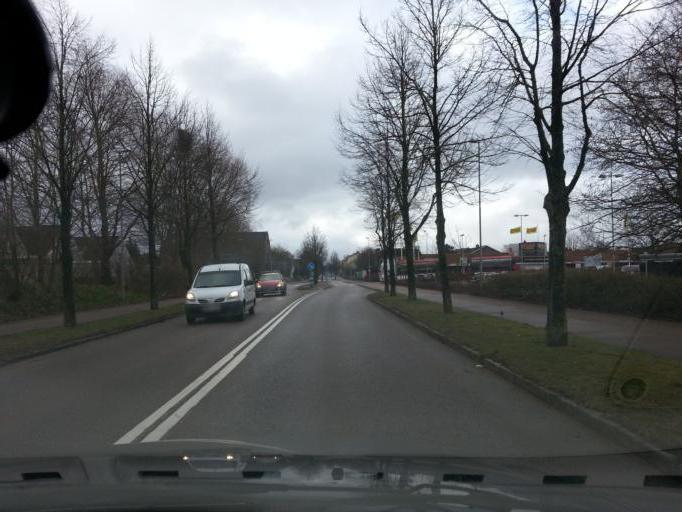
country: SE
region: Skane
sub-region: Astorps Kommun
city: Astorp
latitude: 56.1382
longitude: 12.9422
